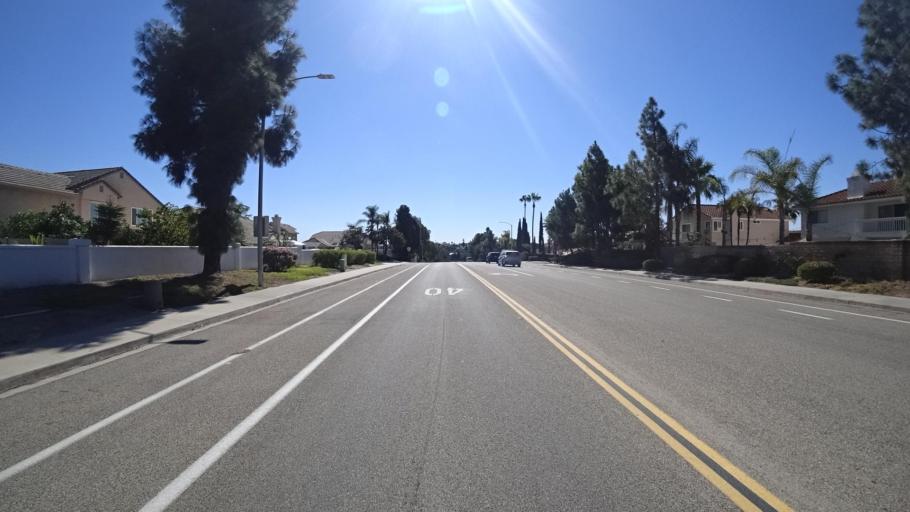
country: US
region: California
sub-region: San Diego County
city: Bonita
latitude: 32.6535
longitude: -116.9899
